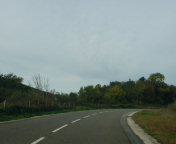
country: FR
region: Bourgogne
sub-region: Departement de Saone-et-Loire
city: Cuiseaux
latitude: 46.4609
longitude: 5.4357
